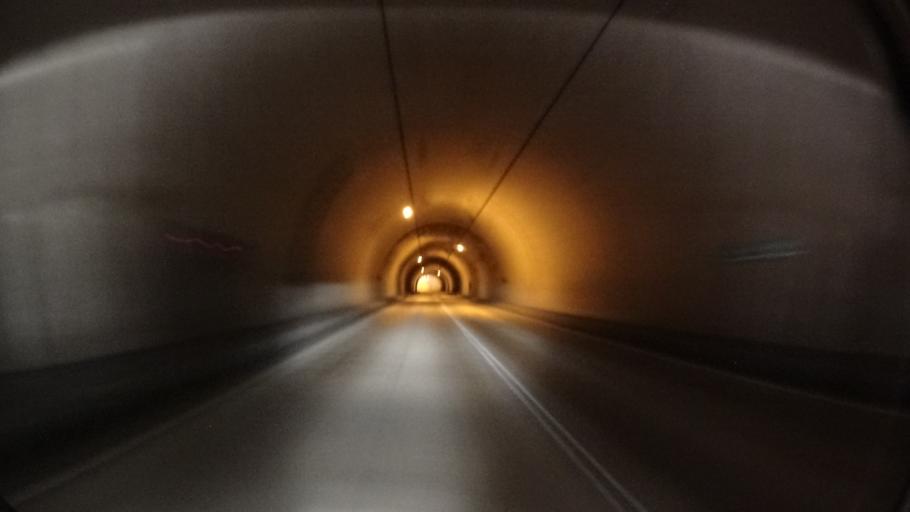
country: JP
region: Hyogo
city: Toyooka
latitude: 35.4999
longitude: 134.9104
